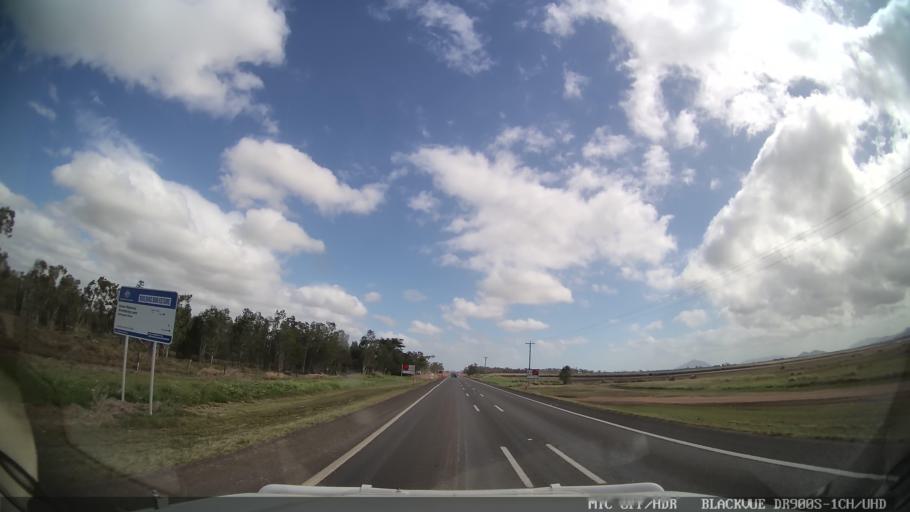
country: AU
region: Queensland
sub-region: Whitsunday
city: Red Hill
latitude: -20.2995
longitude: 148.5097
